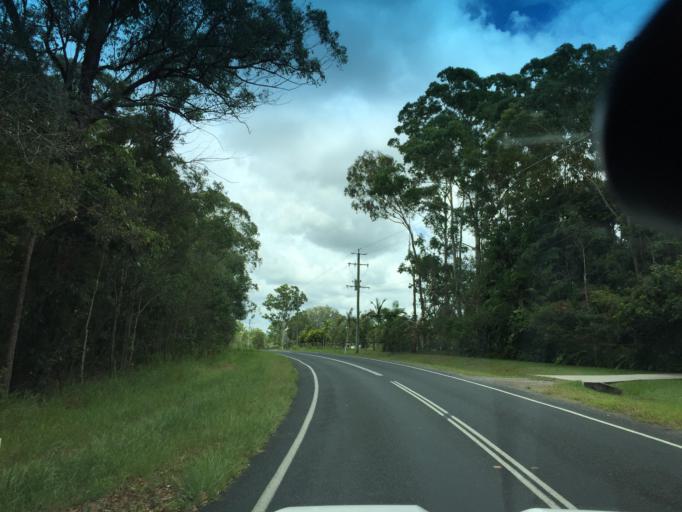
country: AU
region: Queensland
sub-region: Moreton Bay
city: Caboolture
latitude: -27.0444
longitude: 152.9151
